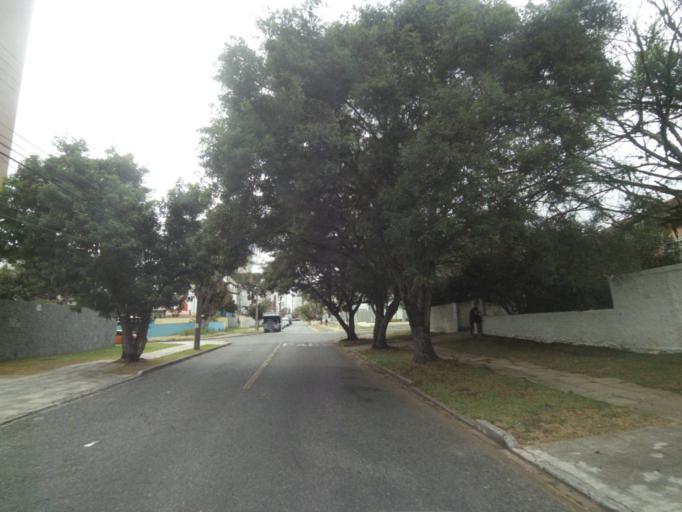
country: BR
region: Parana
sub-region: Curitiba
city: Curitiba
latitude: -25.4599
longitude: -49.2955
